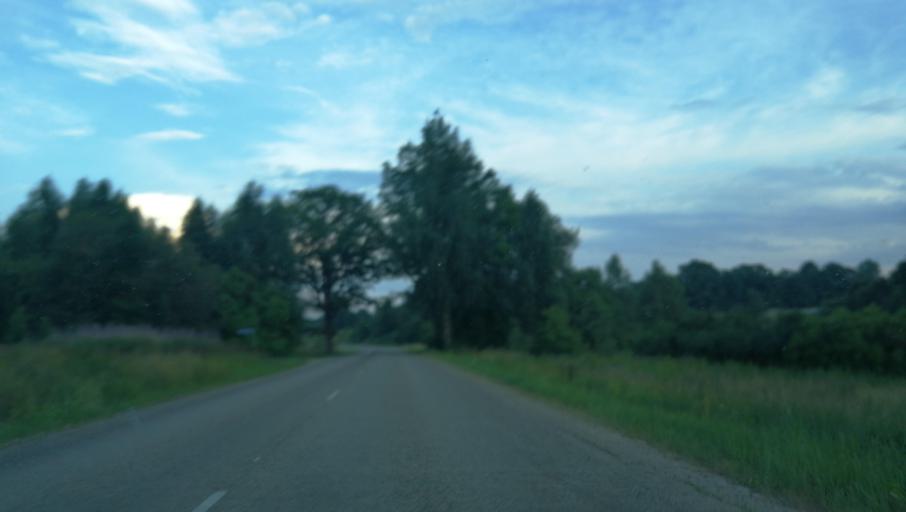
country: LV
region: Priekuli
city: Priekuli
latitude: 57.2624
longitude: 25.3563
